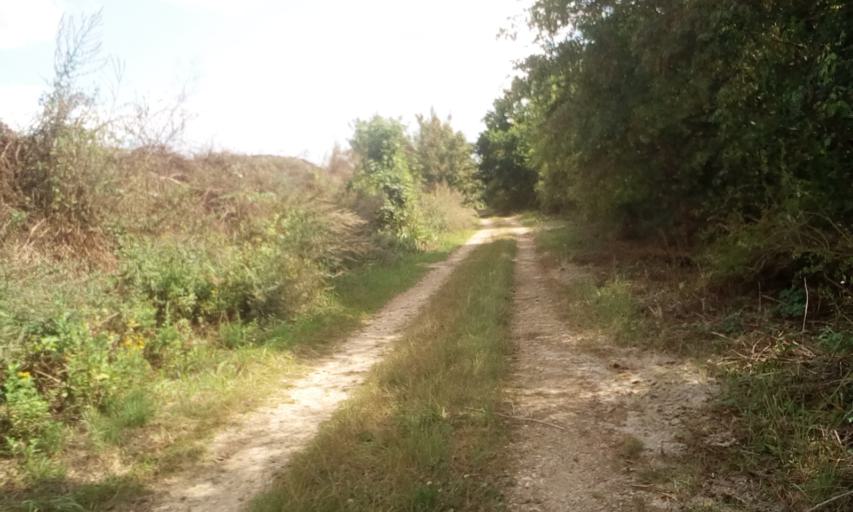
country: FR
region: Lower Normandy
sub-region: Departement du Calvados
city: Cagny
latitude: 49.1153
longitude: -0.2564
